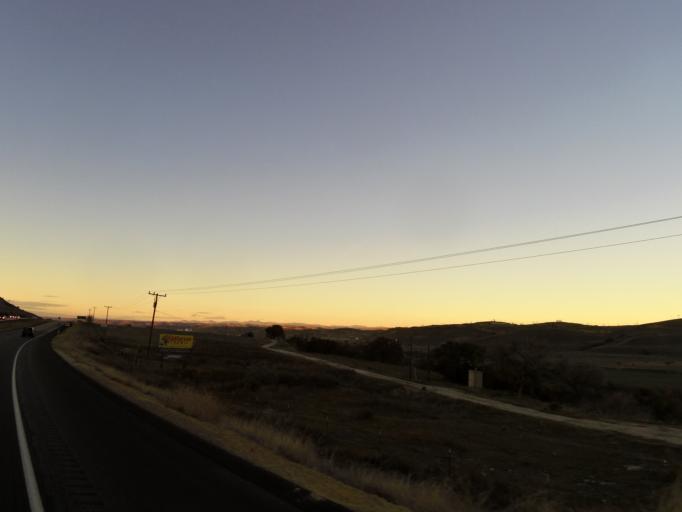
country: US
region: California
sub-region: San Luis Obispo County
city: Lake Nacimiento
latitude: 35.9273
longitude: -120.8692
